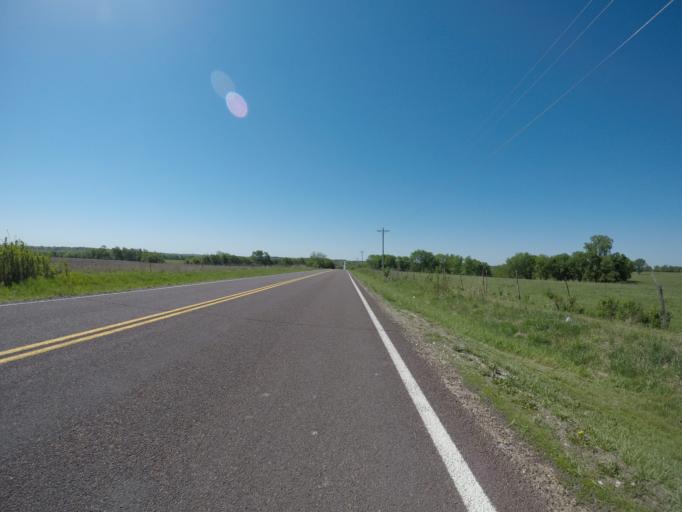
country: US
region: Kansas
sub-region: Osage County
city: Overbrook
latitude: 38.8504
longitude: -95.4821
